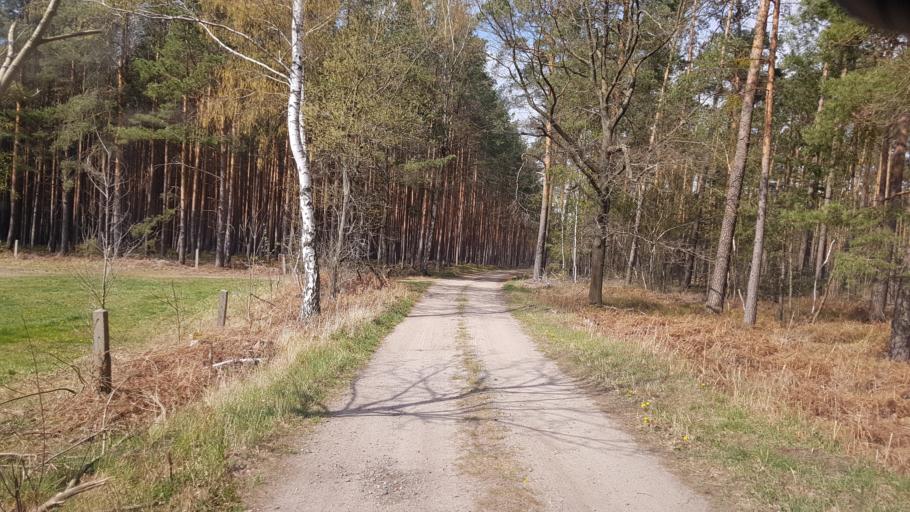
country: DE
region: Brandenburg
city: Ruckersdorf
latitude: 51.5545
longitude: 13.6285
